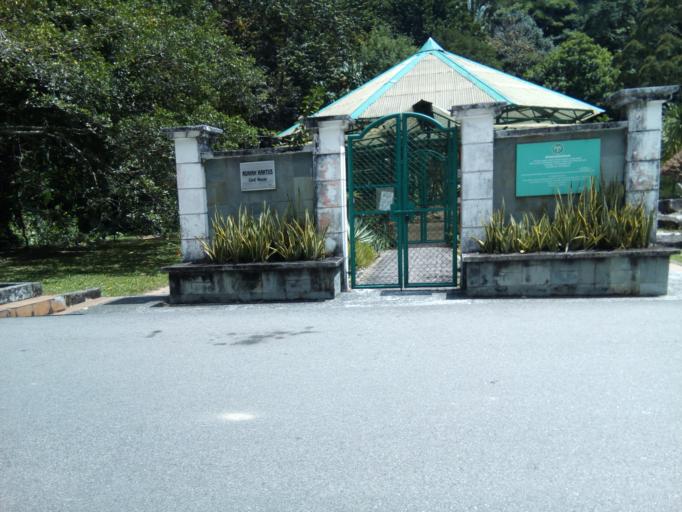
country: MY
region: Penang
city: Tanjung Tokong
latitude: 5.4398
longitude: 100.2888
